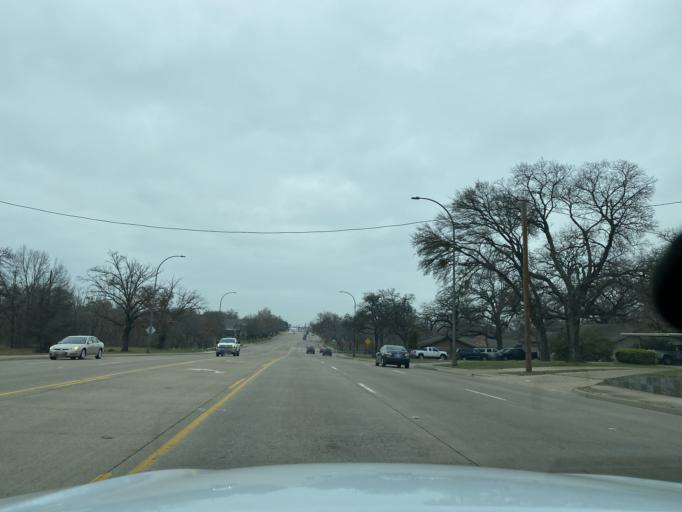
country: US
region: Texas
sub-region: Tarrant County
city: Arlington
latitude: 32.7294
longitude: -97.0974
